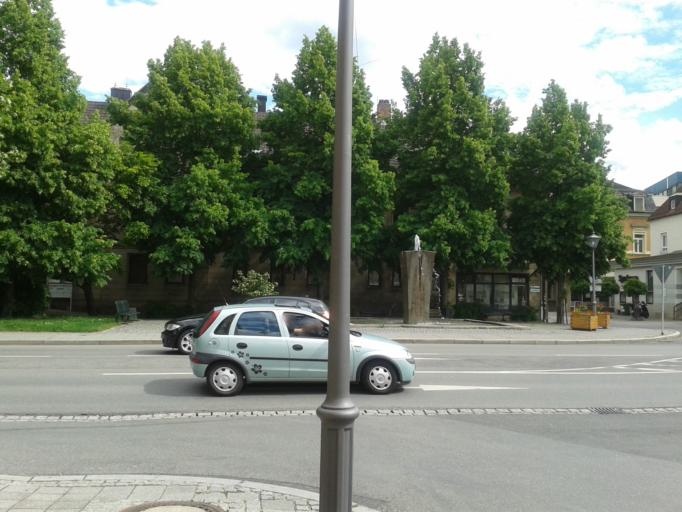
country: DE
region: Bavaria
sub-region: Upper Franconia
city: Lichtenfels
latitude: 50.1462
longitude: 11.0603
